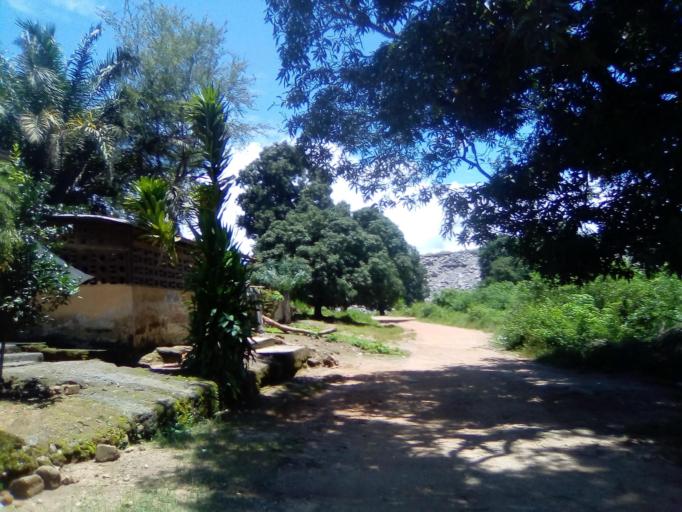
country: SL
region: Eastern Province
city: Koidu
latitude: 8.6362
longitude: -10.9747
